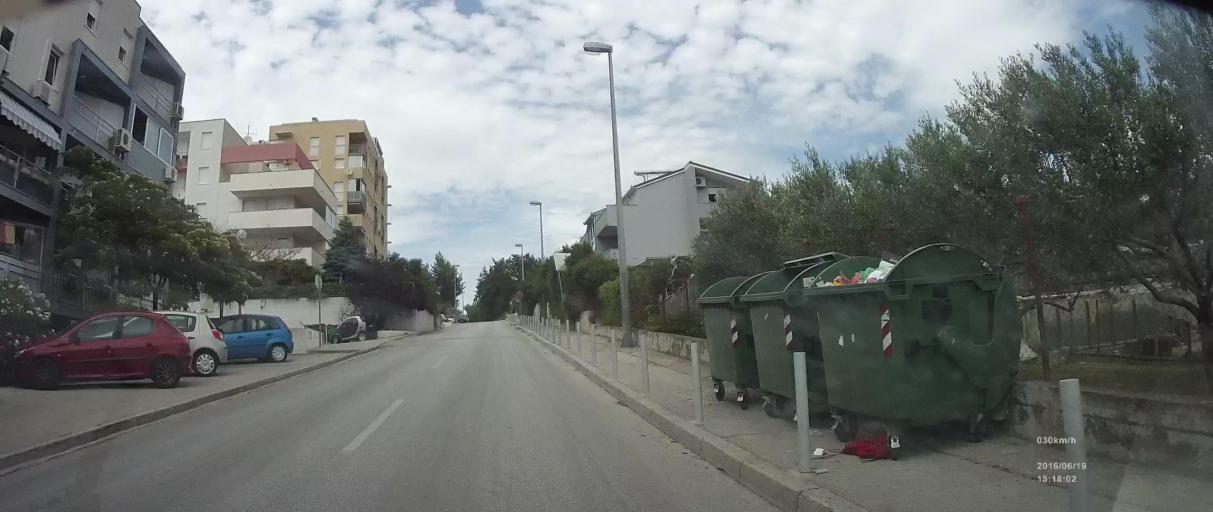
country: HR
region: Splitsko-Dalmatinska
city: Kamen
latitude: 43.5065
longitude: 16.4958
